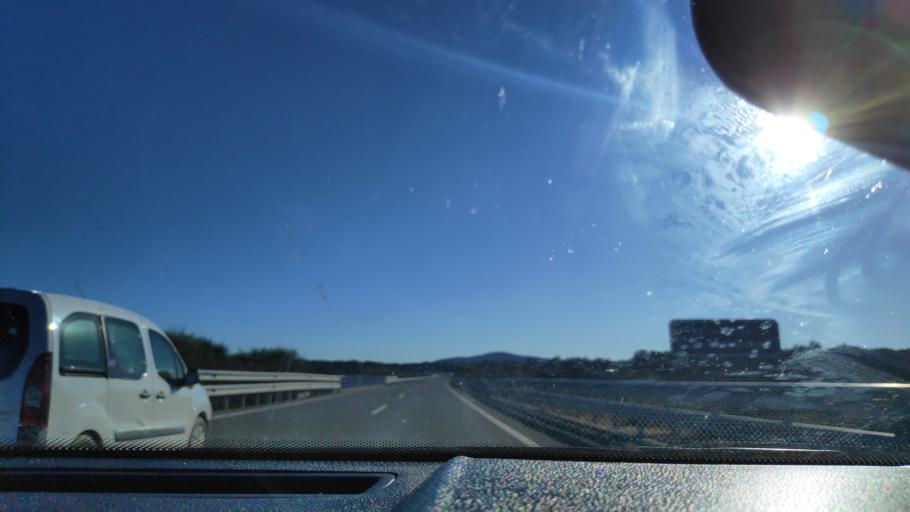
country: ES
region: Andalusia
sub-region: Provincia de Huelva
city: Santa Olalla del Cala
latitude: 37.9826
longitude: -6.2335
